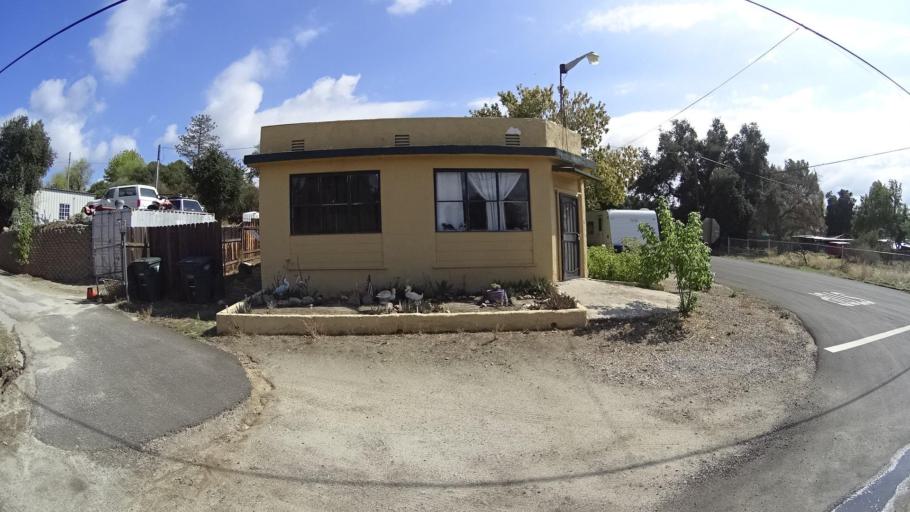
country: US
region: California
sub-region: San Diego County
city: Campo
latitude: 32.6800
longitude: -116.5039
